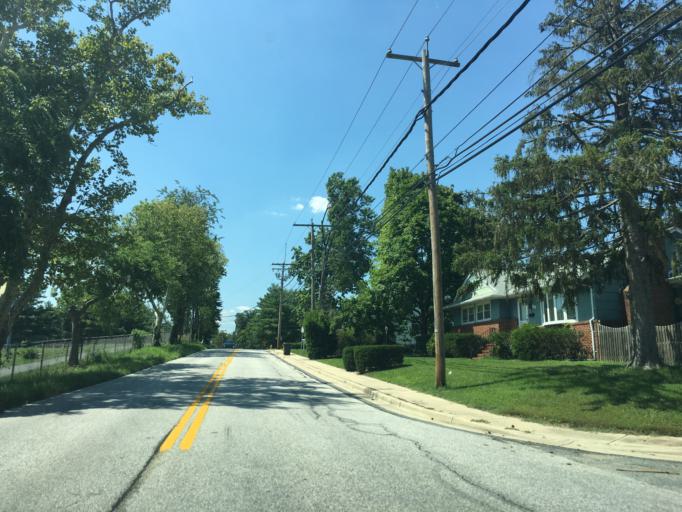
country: US
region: Maryland
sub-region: Anne Arundel County
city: Linthicum
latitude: 39.1984
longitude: -76.6670
